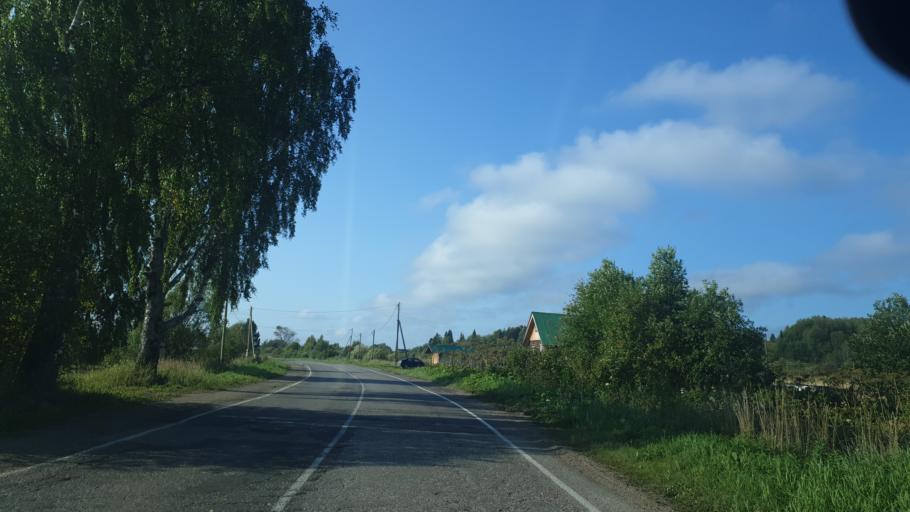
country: RU
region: Komi Republic
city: Vizinga
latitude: 60.9296
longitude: 50.2226
